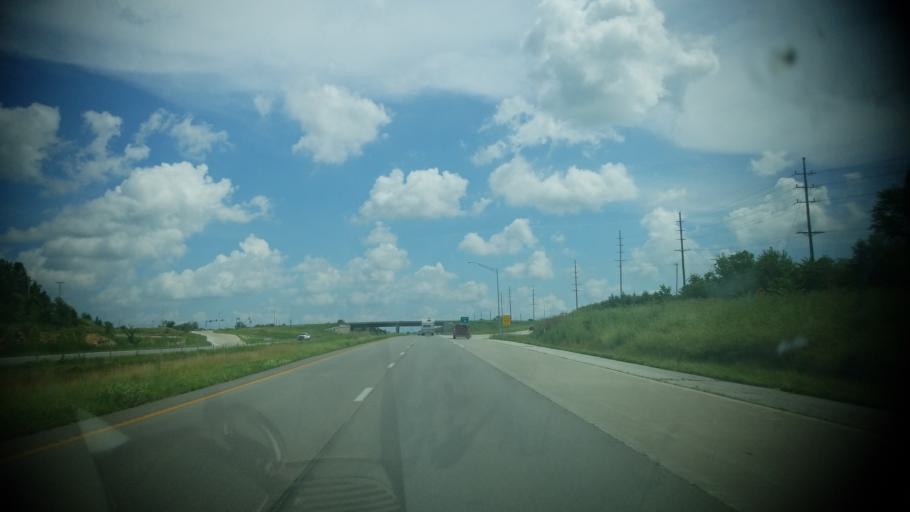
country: US
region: Missouri
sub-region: Lincoln County
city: Moscow Mills
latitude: 38.9124
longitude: -90.9242
